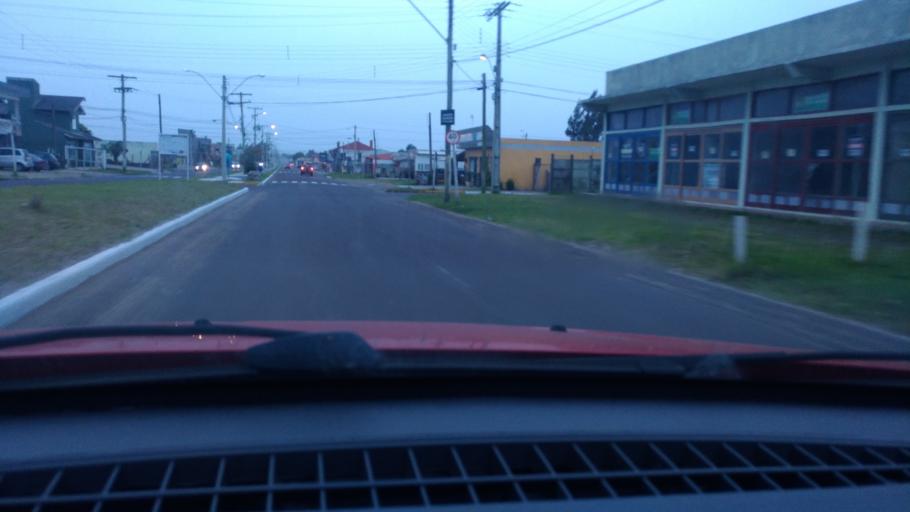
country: BR
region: Rio Grande do Sul
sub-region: Capao Da Canoa
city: Capao da Canoa
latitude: -29.8505
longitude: -50.0731
